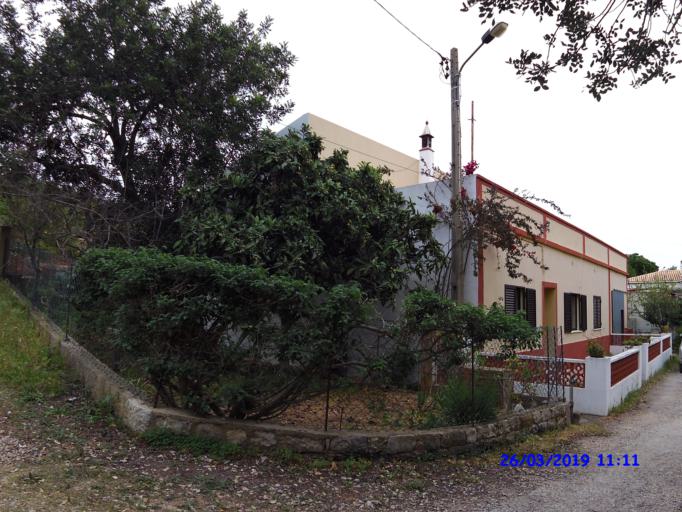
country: PT
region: Faro
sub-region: Loule
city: Boliqueime
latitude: 37.1652
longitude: -8.1977
